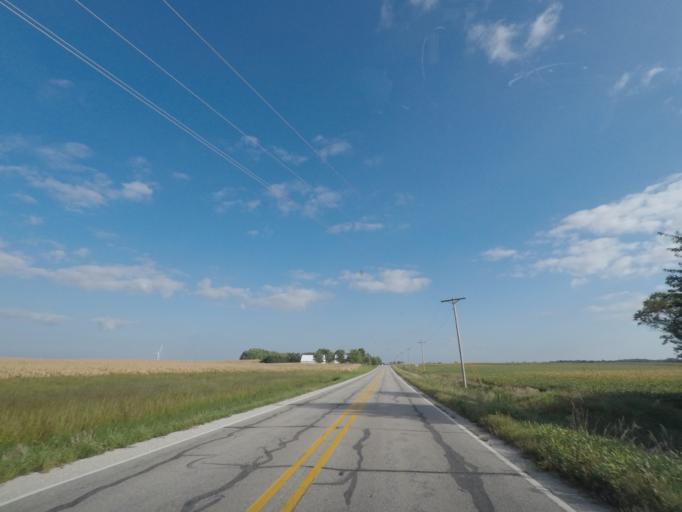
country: US
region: Iowa
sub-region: Story County
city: Nevada
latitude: 41.9839
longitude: -93.4630
